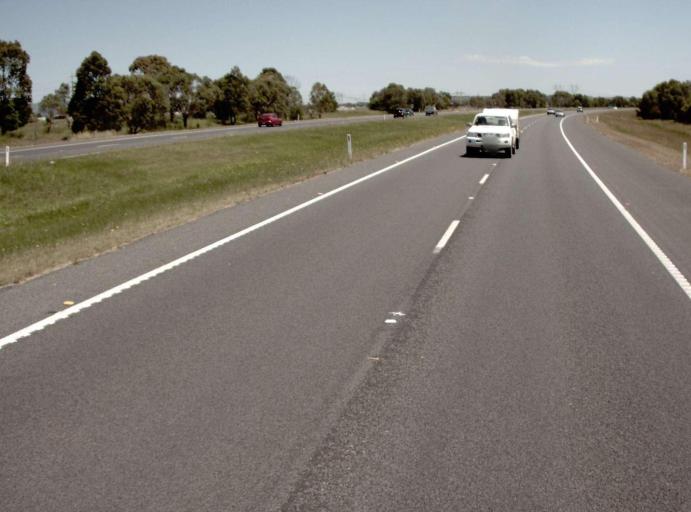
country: AU
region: Victoria
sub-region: Latrobe
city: Morwell
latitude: -38.2395
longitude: 146.4485
